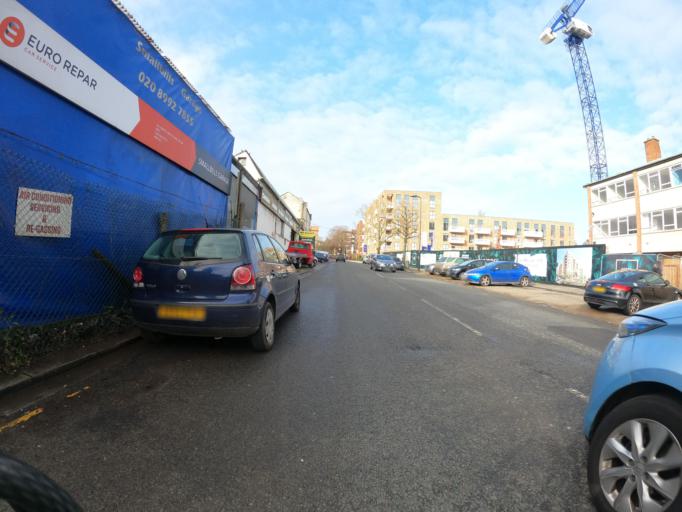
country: GB
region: England
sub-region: Greater London
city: Acton
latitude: 51.5016
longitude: -0.2783
